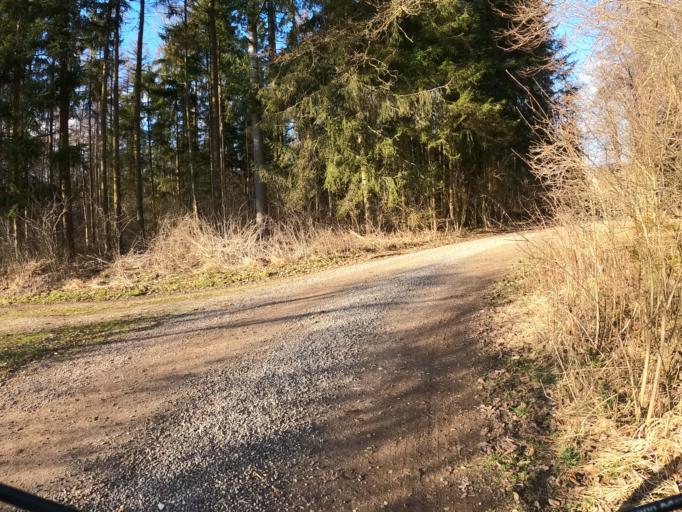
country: DE
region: Bavaria
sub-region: Swabia
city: Leipheim
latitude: 48.4205
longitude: 10.2223
